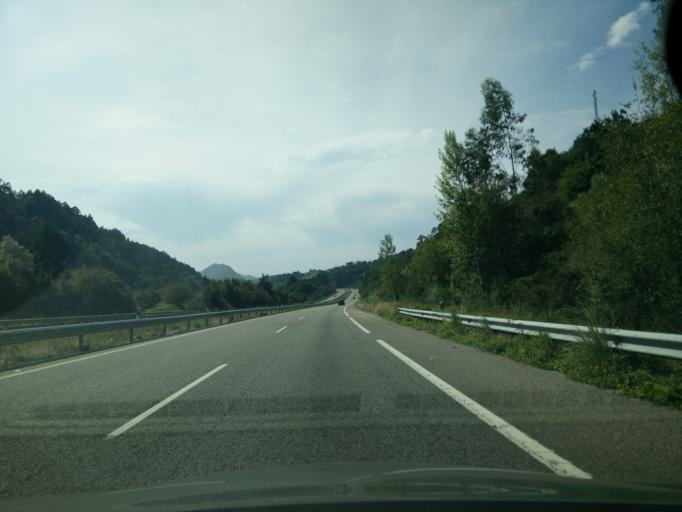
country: ES
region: Asturias
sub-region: Province of Asturias
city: Ribadesella
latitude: 43.4365
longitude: -5.0692
